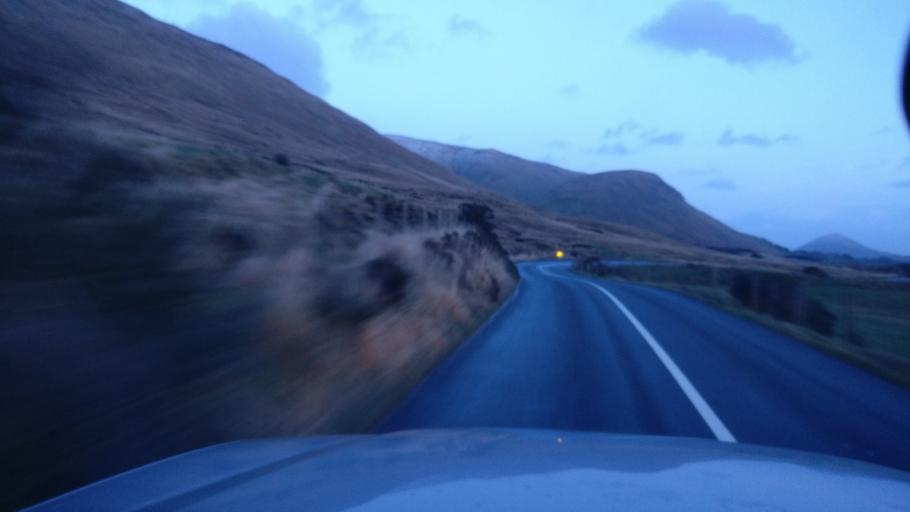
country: IE
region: Connaught
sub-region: Maigh Eo
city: Westport
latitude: 53.5583
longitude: -9.6457
